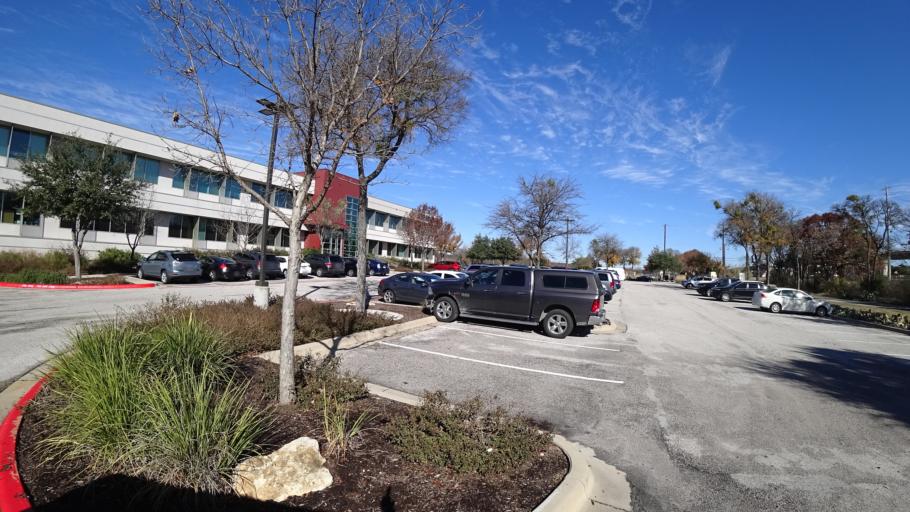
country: US
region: Texas
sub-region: Travis County
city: Wells Branch
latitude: 30.4254
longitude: -97.7039
